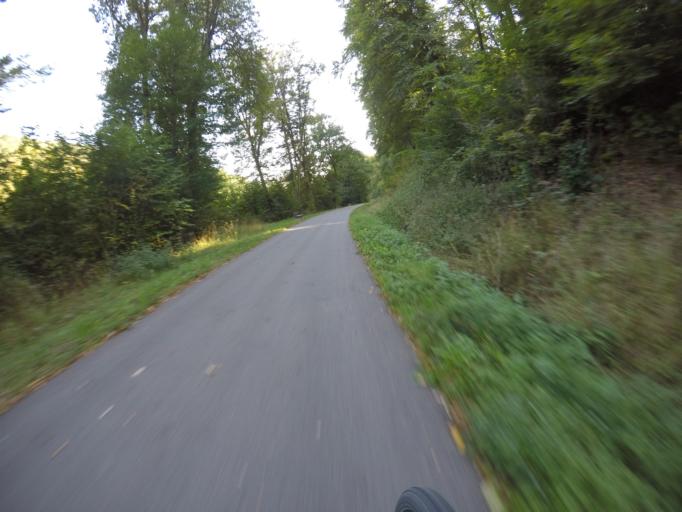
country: DE
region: Baden-Wuerttemberg
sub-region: Regierungsbezirk Stuttgart
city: Waldenbuch
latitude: 48.6420
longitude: 9.1670
